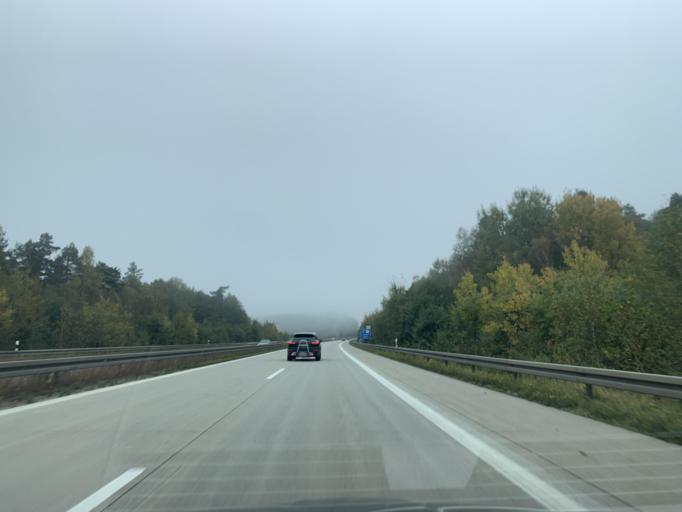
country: DE
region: Bavaria
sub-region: Upper Palatinate
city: Luhe-Wildenau
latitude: 49.5583
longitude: 12.1225
